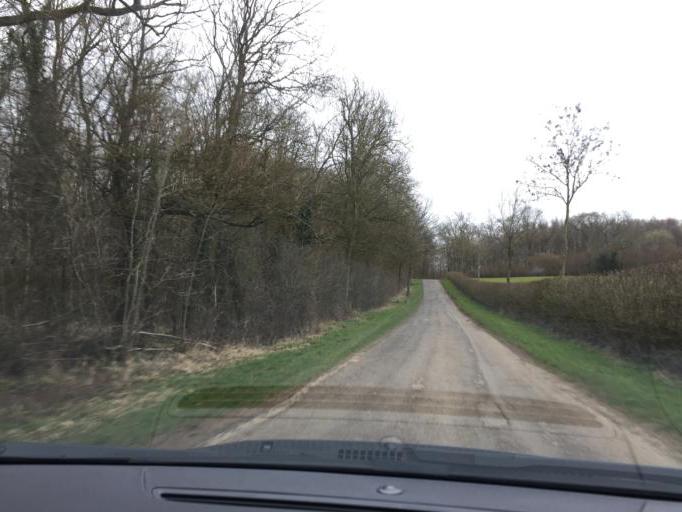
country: GB
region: England
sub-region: Oxfordshire
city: Deddington
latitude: 51.9502
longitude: -1.3713
